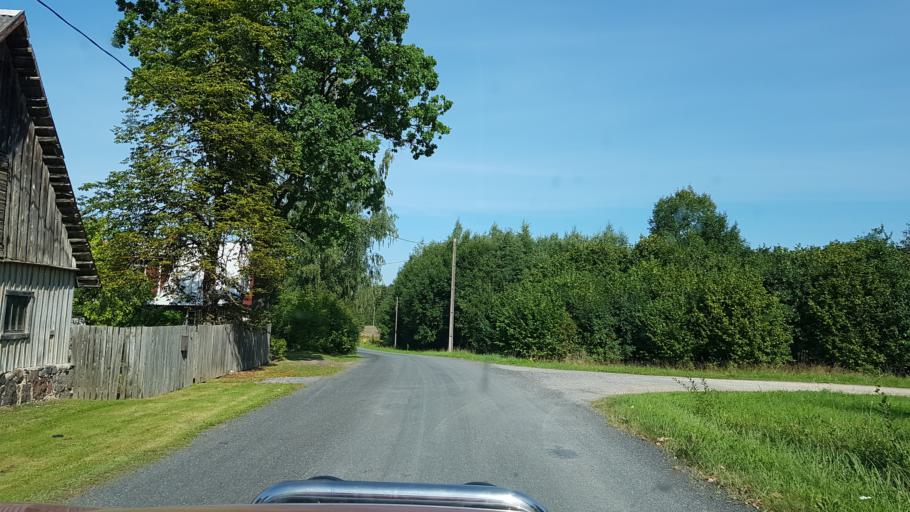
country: EE
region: Viljandimaa
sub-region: Viljandi linn
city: Viljandi
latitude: 58.4115
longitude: 25.5256
